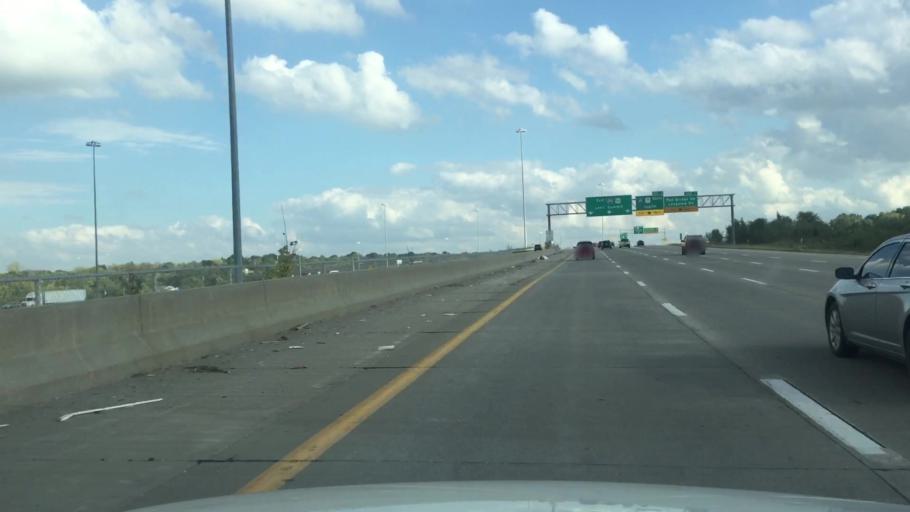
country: US
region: Missouri
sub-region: Jackson County
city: Grandview
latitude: 38.9367
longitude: -94.5347
